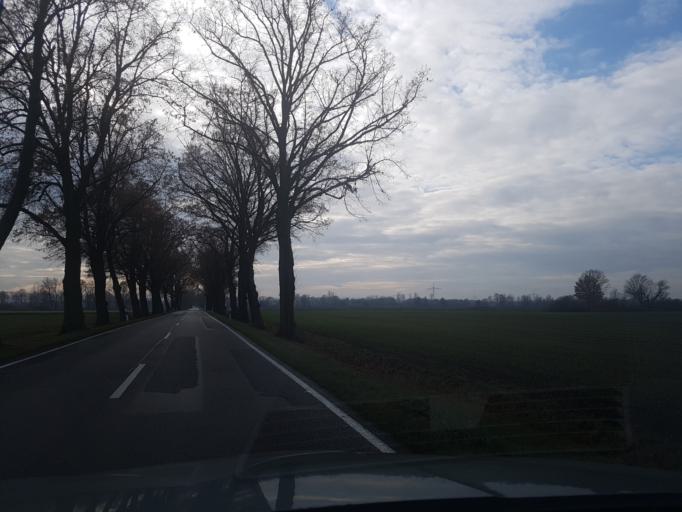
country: DE
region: Brandenburg
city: Plessa
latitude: 51.4531
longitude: 13.6226
